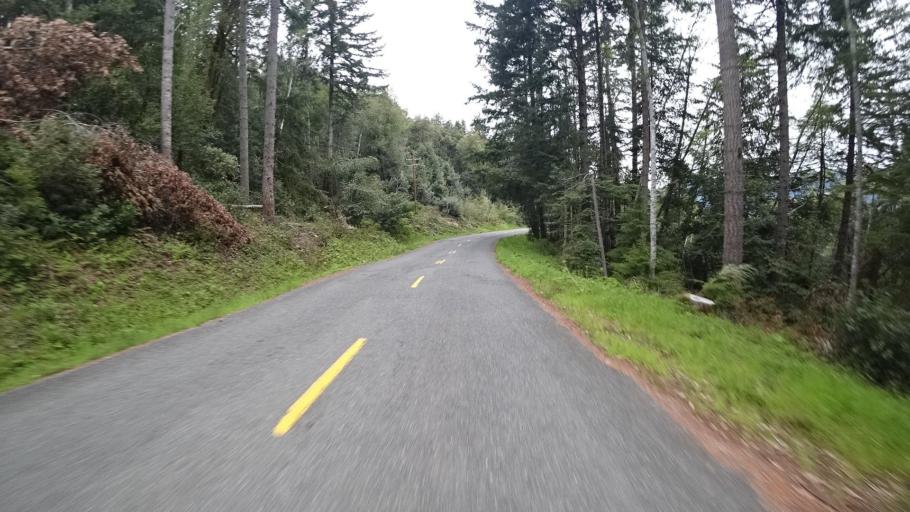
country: US
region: California
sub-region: Humboldt County
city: Blue Lake
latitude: 40.9302
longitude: -123.8446
